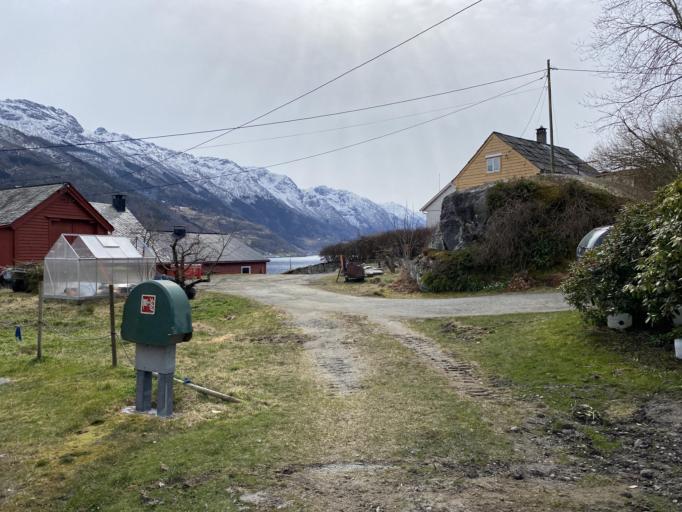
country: NO
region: Hordaland
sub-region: Ullensvang
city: Kinsarvik
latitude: 60.3000
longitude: 6.6023
